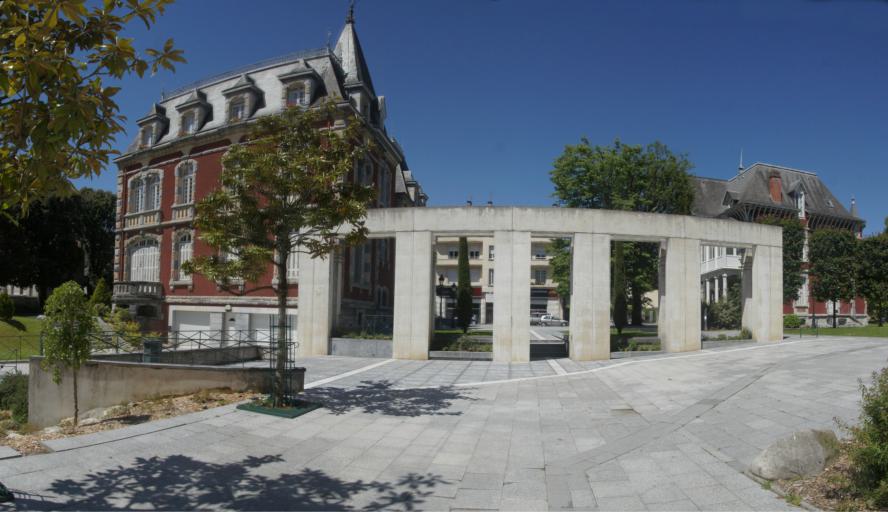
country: FR
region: Midi-Pyrenees
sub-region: Departement des Hautes-Pyrenees
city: Lourdes
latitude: 43.0919
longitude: -0.0456
